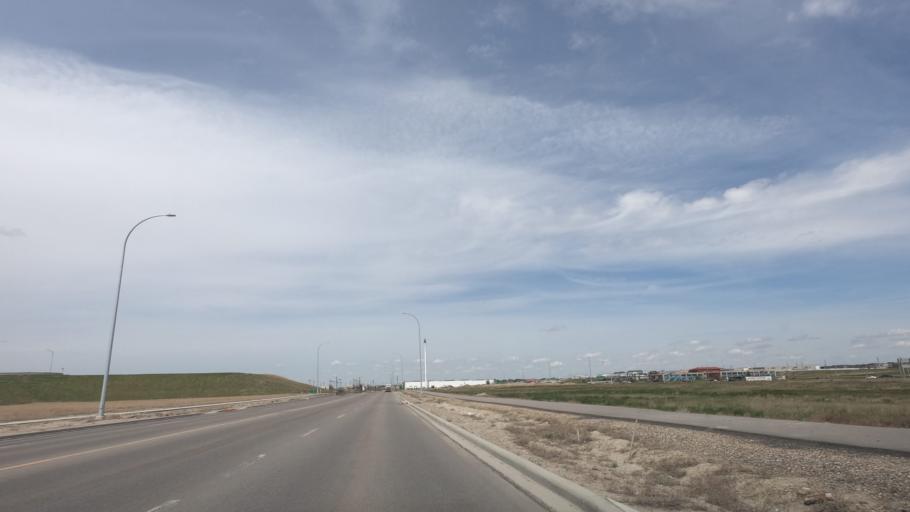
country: CA
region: Alberta
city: Airdrie
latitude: 51.2543
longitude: -114.0050
